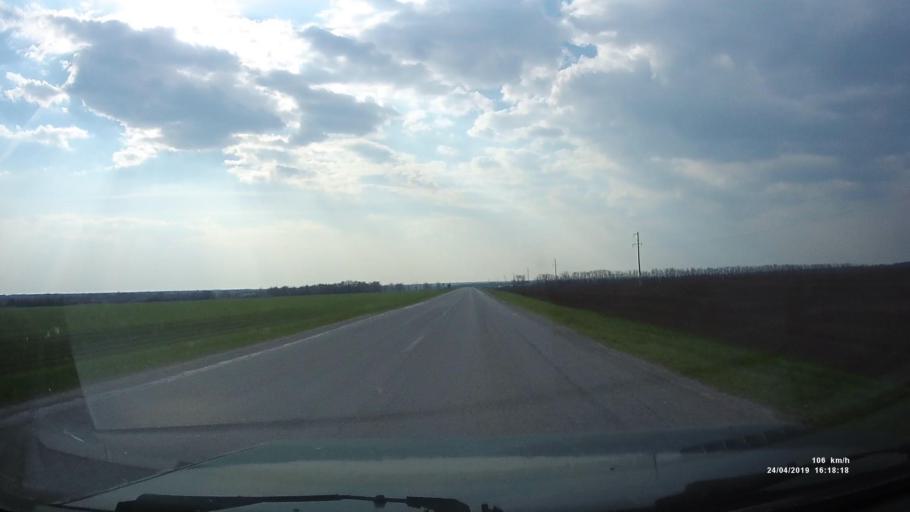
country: RU
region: Rostov
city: Sovetskoye
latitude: 46.7738
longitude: 42.1189
